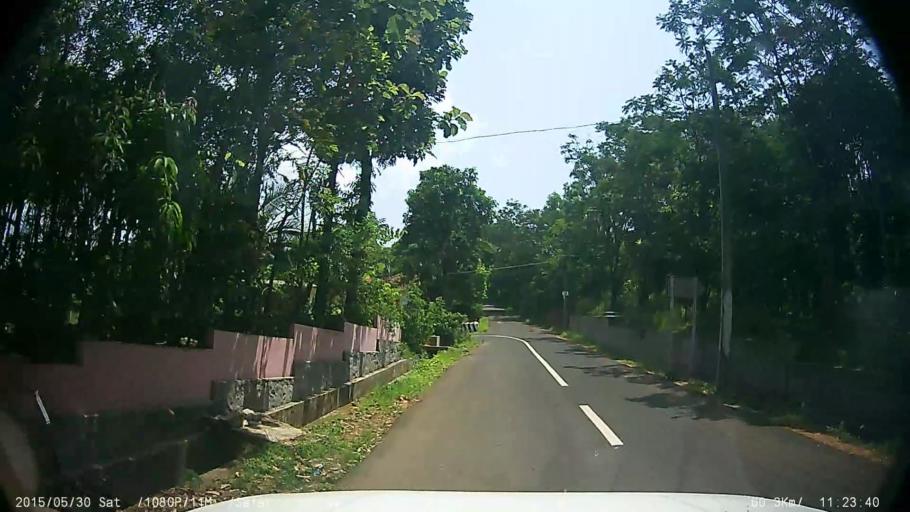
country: IN
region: Kerala
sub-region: Wayanad
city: Panamaram
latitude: 11.8027
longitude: 76.0281
